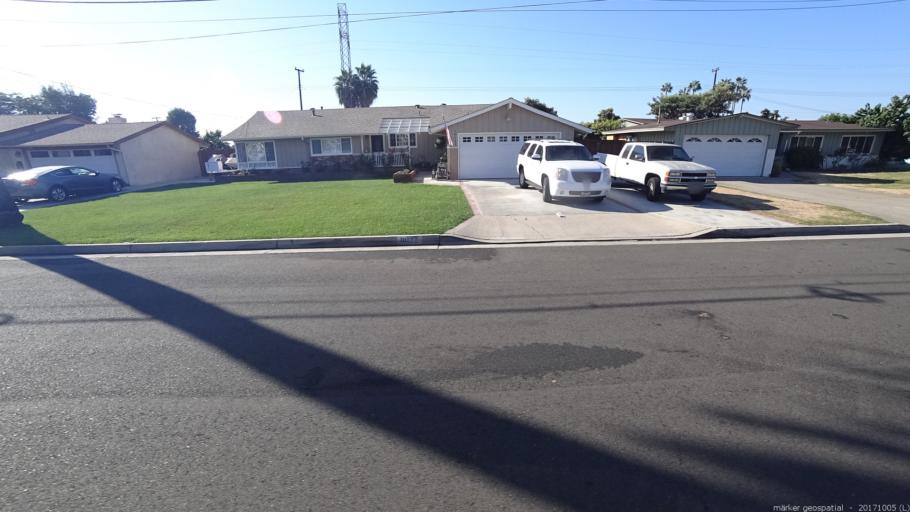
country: US
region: California
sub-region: Orange County
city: Garden Grove
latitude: 33.7982
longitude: -117.9565
